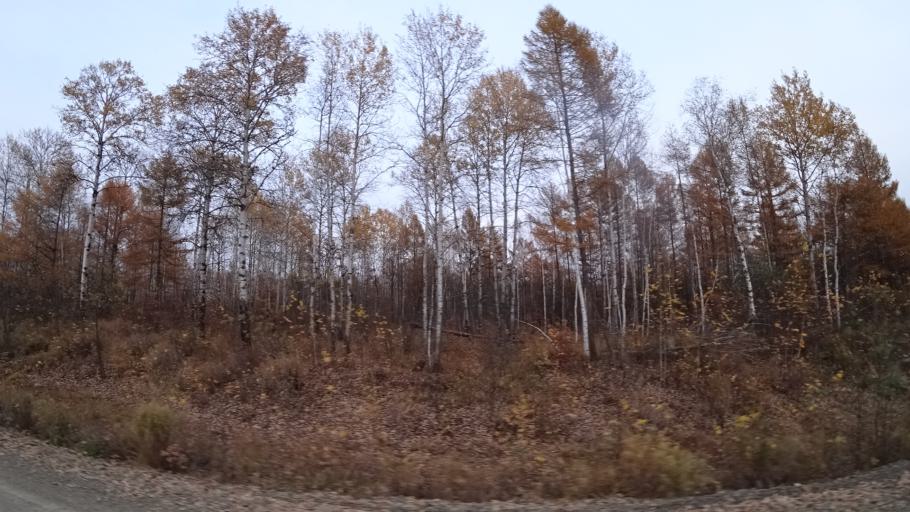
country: RU
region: Khabarovsk Krai
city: Amursk
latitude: 49.9825
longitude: 136.3147
